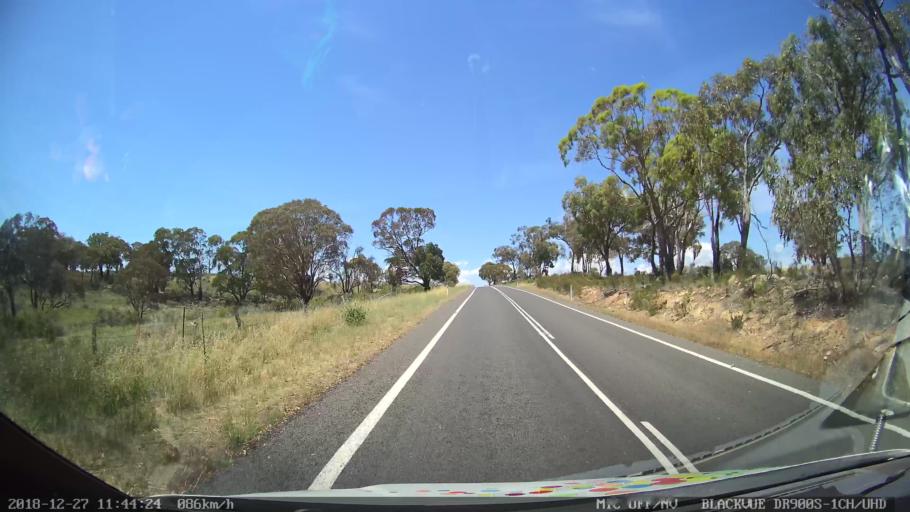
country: AU
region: New South Wales
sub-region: Bathurst Regional
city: Perthville
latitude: -33.5714
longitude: 149.4751
